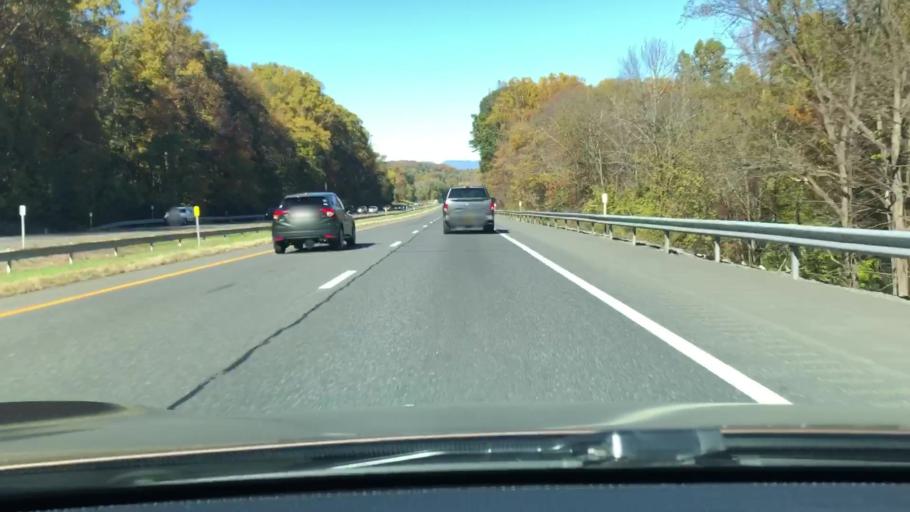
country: US
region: New York
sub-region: Ulster County
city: Tillson
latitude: 41.8387
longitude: -74.0579
